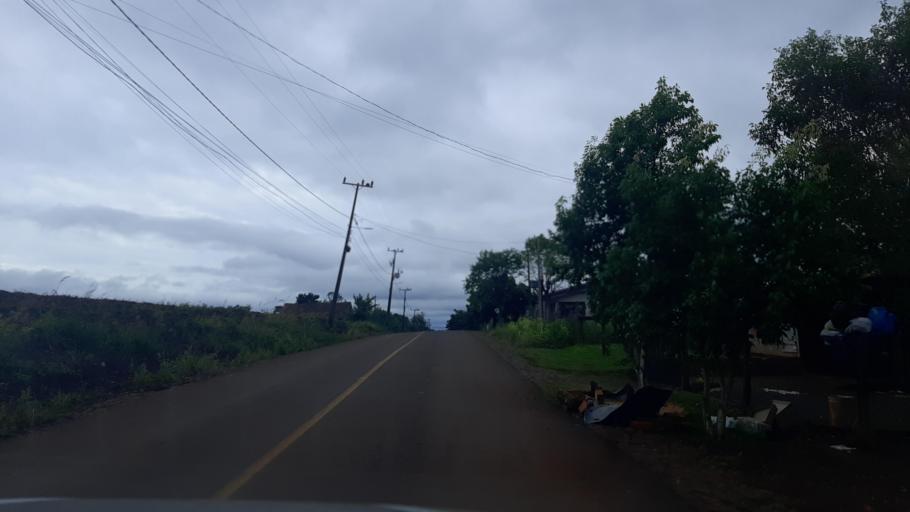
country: BR
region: Parana
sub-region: Ampere
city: Ampere
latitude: -26.0373
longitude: -53.5065
